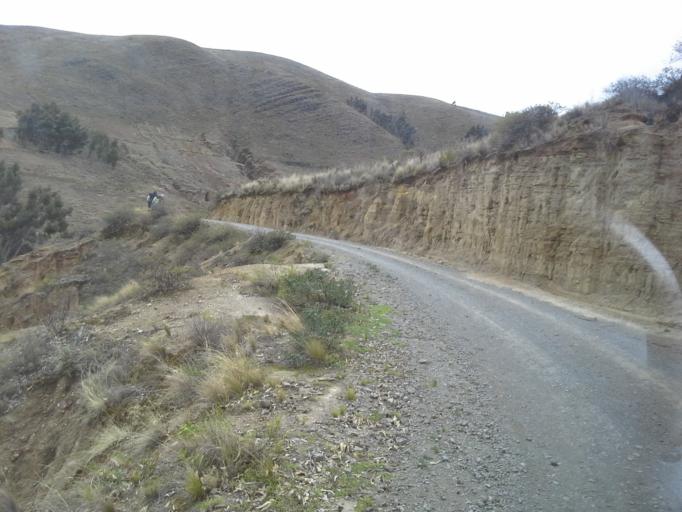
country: BO
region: Cochabamba
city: Colomi
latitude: -17.4151
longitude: -65.8048
